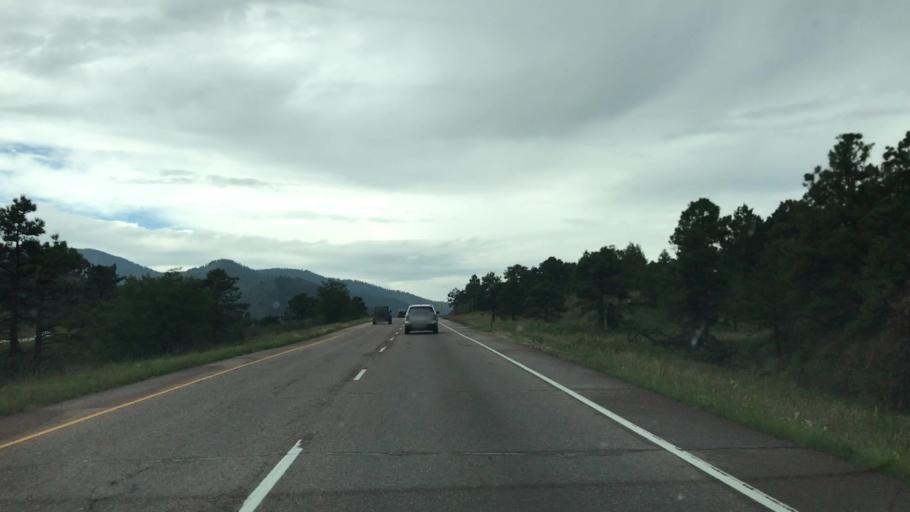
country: US
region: Colorado
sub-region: El Paso County
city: Cascade-Chipita Park
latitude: 38.9333
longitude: -105.0036
